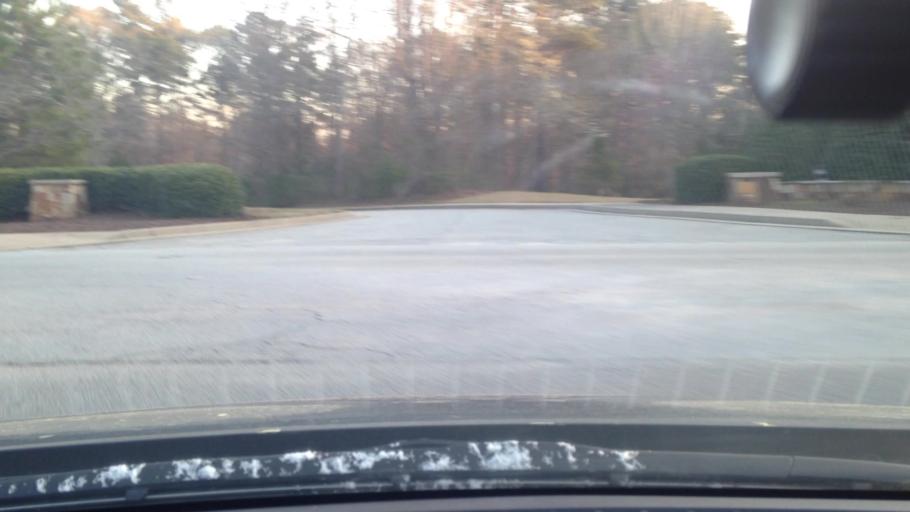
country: US
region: Georgia
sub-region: Coweta County
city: East Newnan
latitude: 33.3774
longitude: -84.7473
